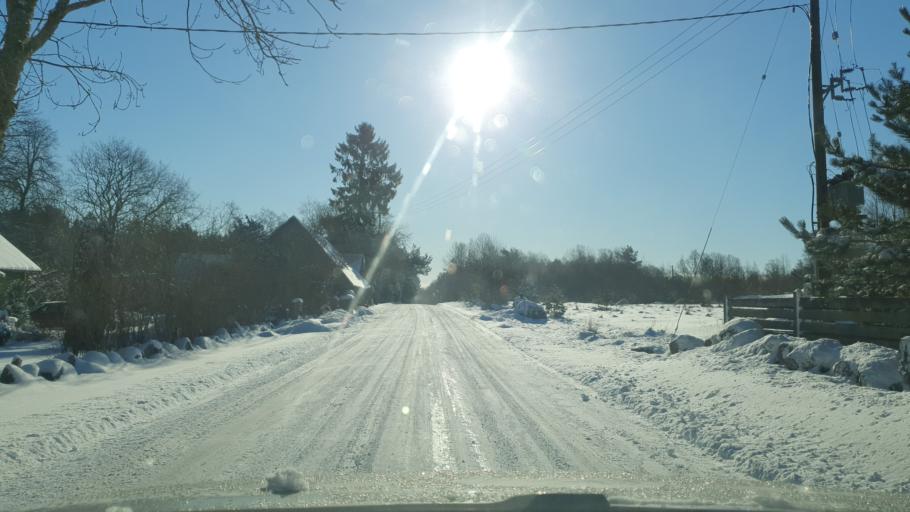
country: EE
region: Harju
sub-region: Kuusalu vald
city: Kuusalu
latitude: 59.4900
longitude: 25.3850
